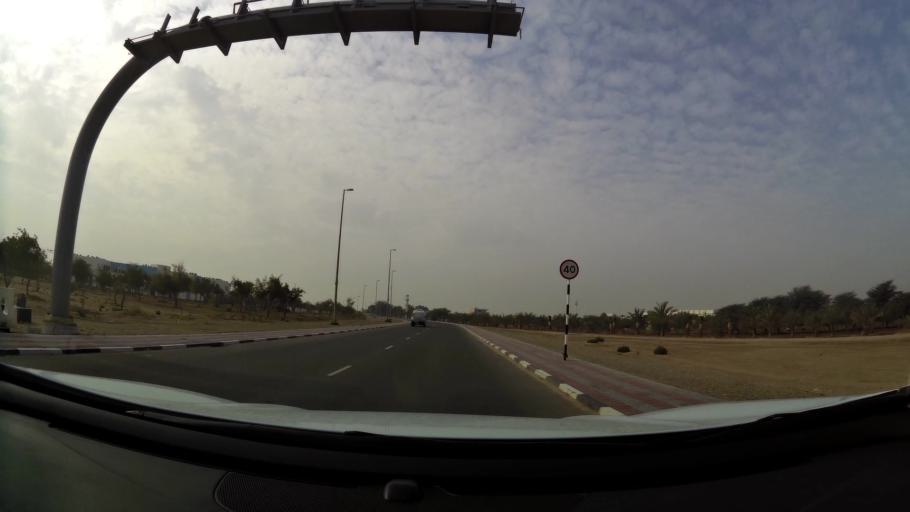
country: AE
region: Abu Dhabi
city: Abu Dhabi
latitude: 24.6837
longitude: 54.7760
